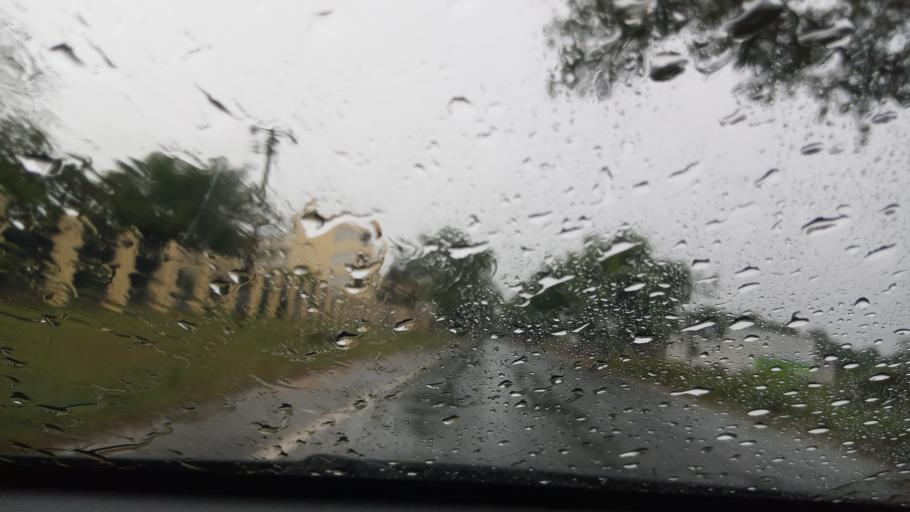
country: IN
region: Tamil Nadu
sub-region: Vellore
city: Kalavai
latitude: 12.8020
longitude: 79.4336
